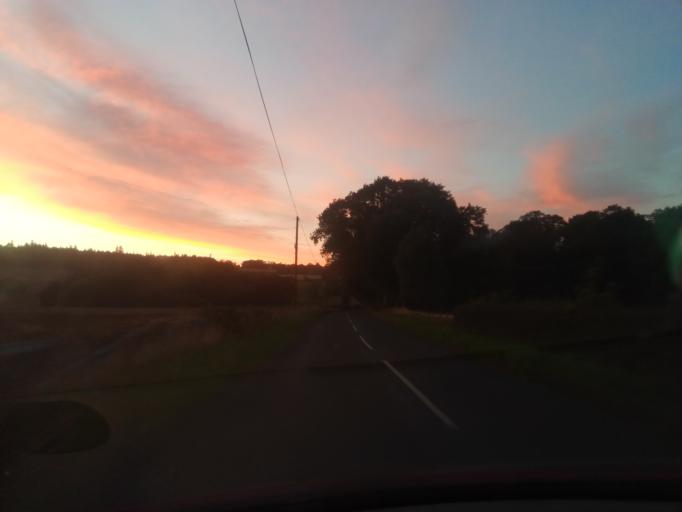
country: GB
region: England
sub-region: Northumberland
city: Wall
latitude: 55.0191
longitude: -2.1504
